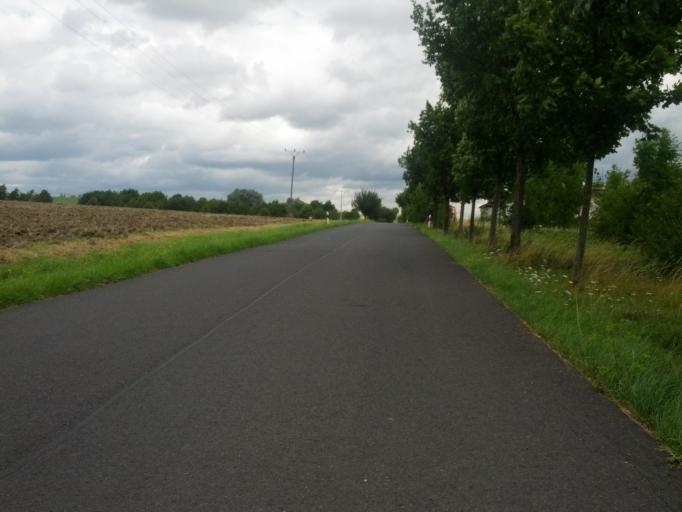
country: DE
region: Thuringia
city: Bischofroda
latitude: 50.9937
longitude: 10.3737
